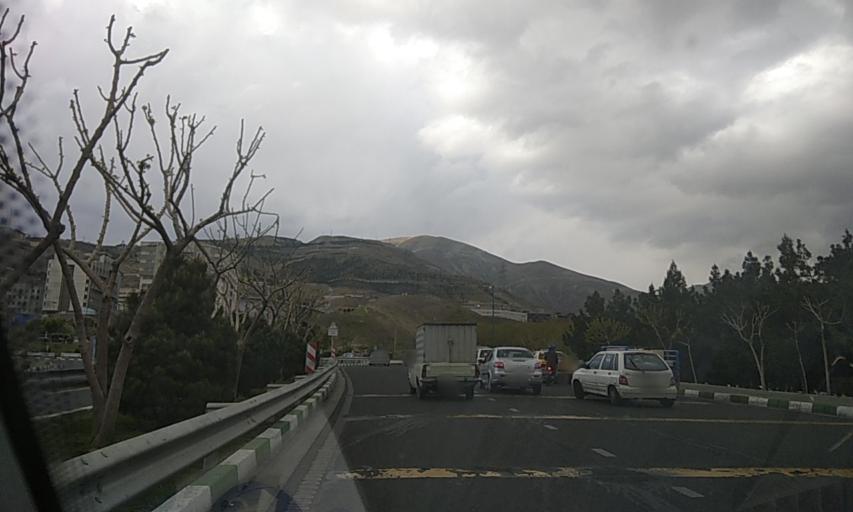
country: IR
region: Tehran
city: Tajrish
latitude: 35.7766
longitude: 51.3202
